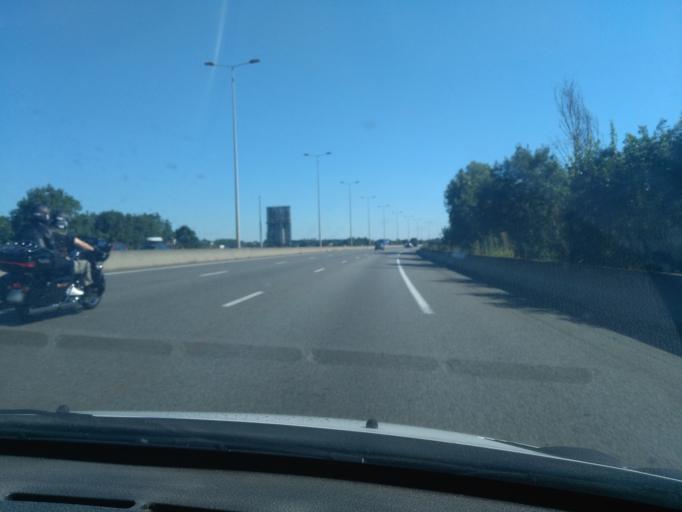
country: FR
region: Rhone-Alpes
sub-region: Departement du Rhone
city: Pommiers
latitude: 45.9549
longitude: 4.7170
